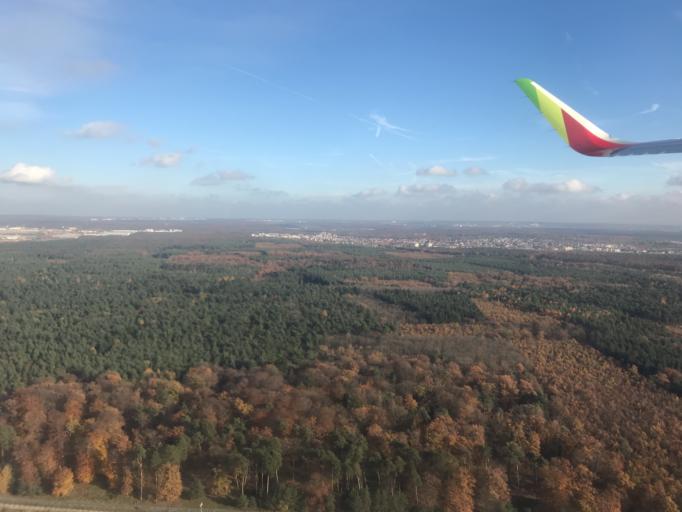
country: DE
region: Hesse
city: Kelsterbach
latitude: 50.0085
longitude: 8.5264
